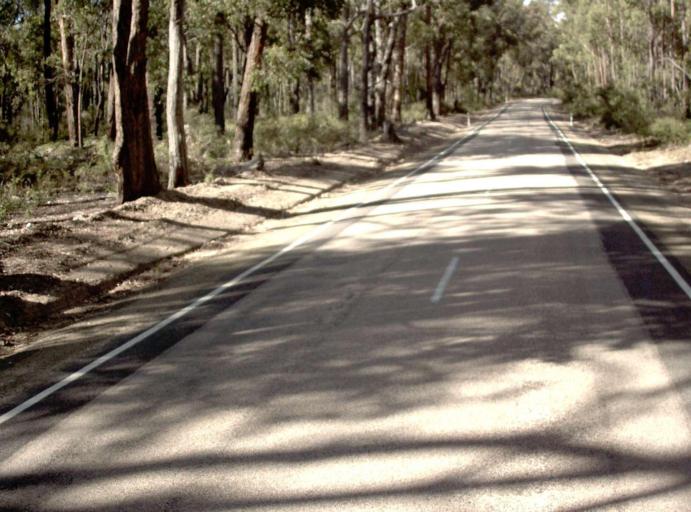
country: AU
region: Victoria
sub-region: East Gippsland
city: Lakes Entrance
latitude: -37.6857
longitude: 148.0499
